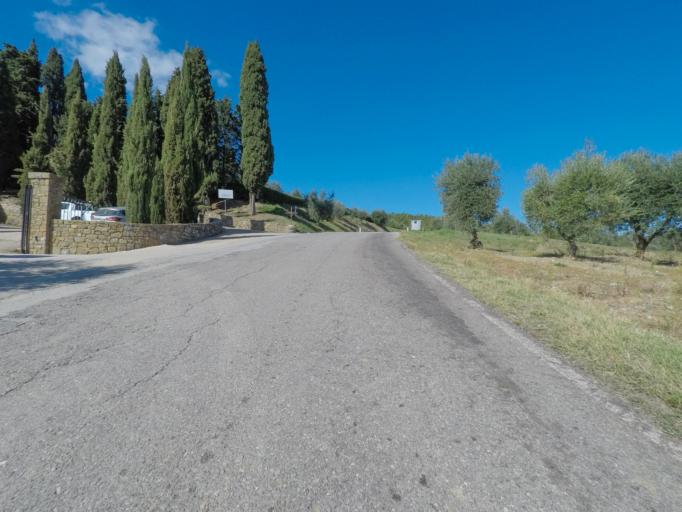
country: IT
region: Tuscany
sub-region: Provincia di Siena
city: Radda in Chianti
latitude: 43.5189
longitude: 11.4039
